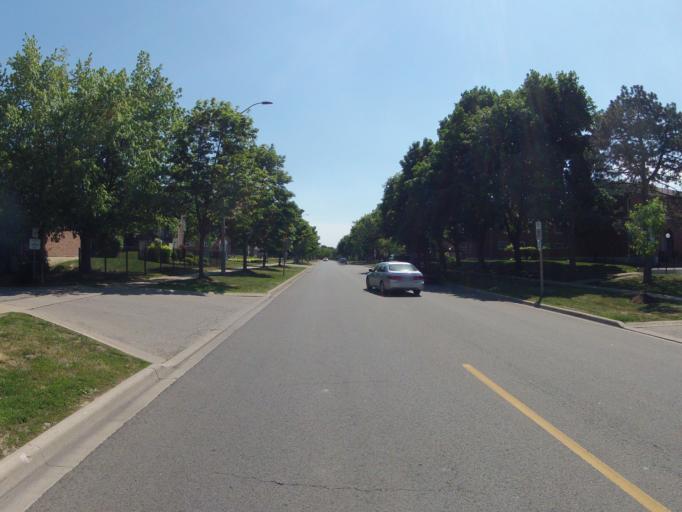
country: CA
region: Ontario
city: Oakville
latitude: 43.5084
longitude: -79.6428
